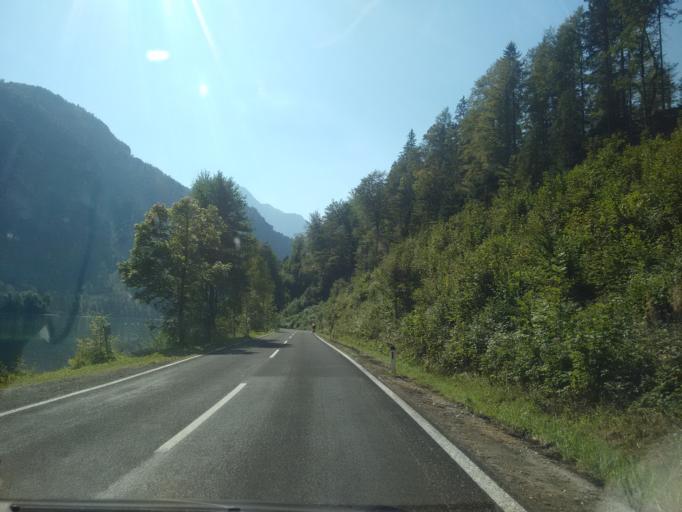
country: AT
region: Upper Austria
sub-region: Politischer Bezirk Gmunden
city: Gruenau im Almtal
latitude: 47.7519
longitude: 13.9515
